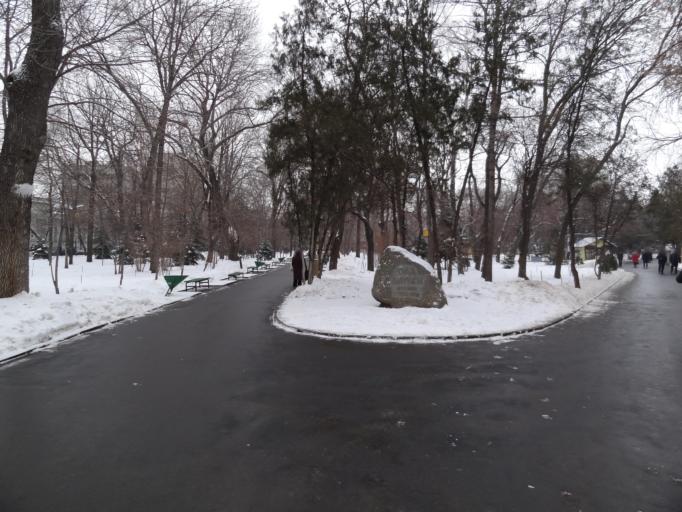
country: RU
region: Saratov
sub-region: Saratovskiy Rayon
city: Saratov
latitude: 51.5296
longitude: 46.0360
